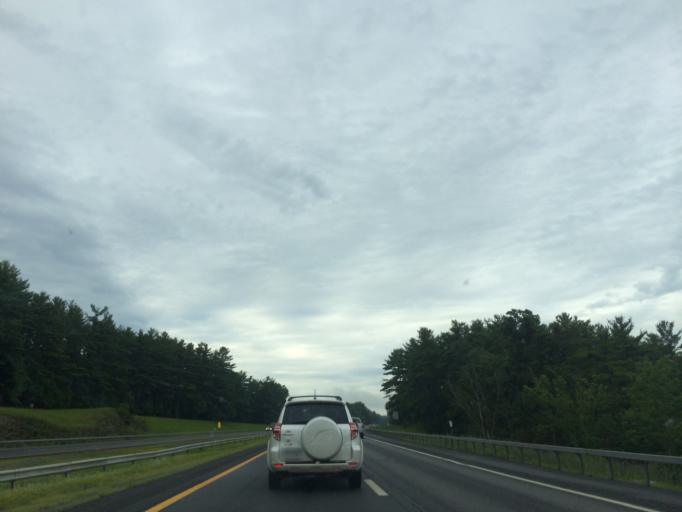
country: US
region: New York
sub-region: Albany County
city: Ravena
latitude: 42.4140
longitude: -73.8098
